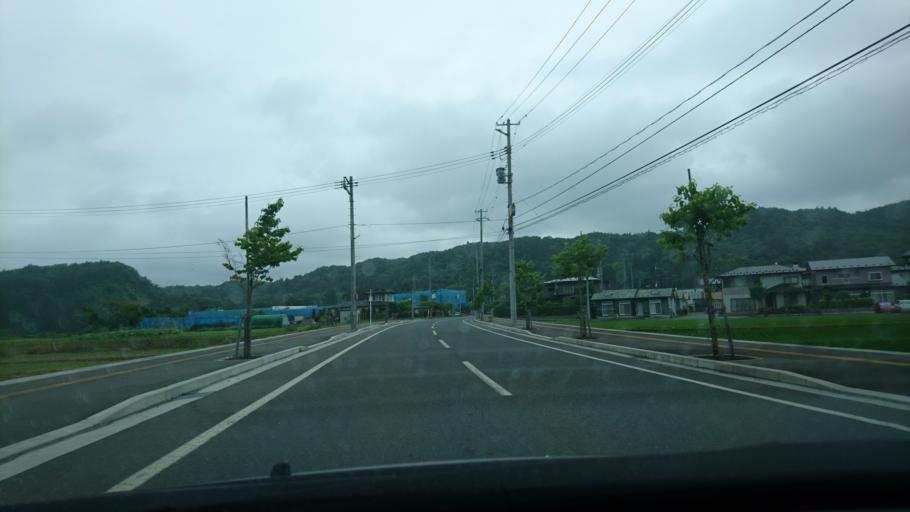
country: JP
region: Iwate
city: Ichinoseki
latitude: 38.9386
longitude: 141.0832
